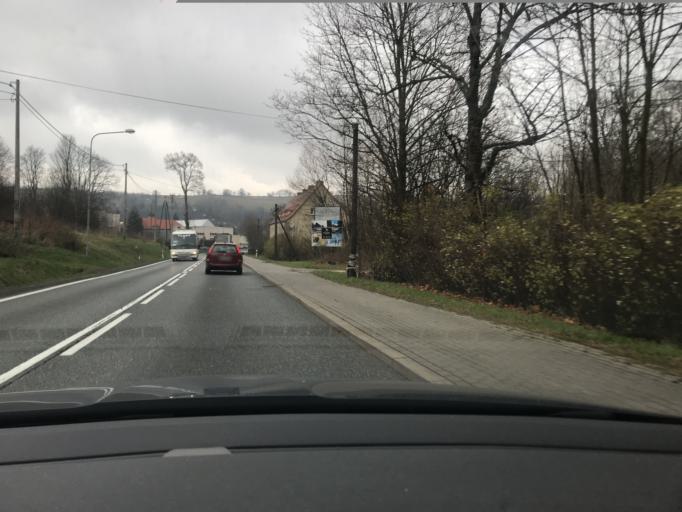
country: PL
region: Lower Silesian Voivodeship
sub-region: Powiat klodzki
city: Duszniki-Zdroj
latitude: 50.4026
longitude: 16.3822
